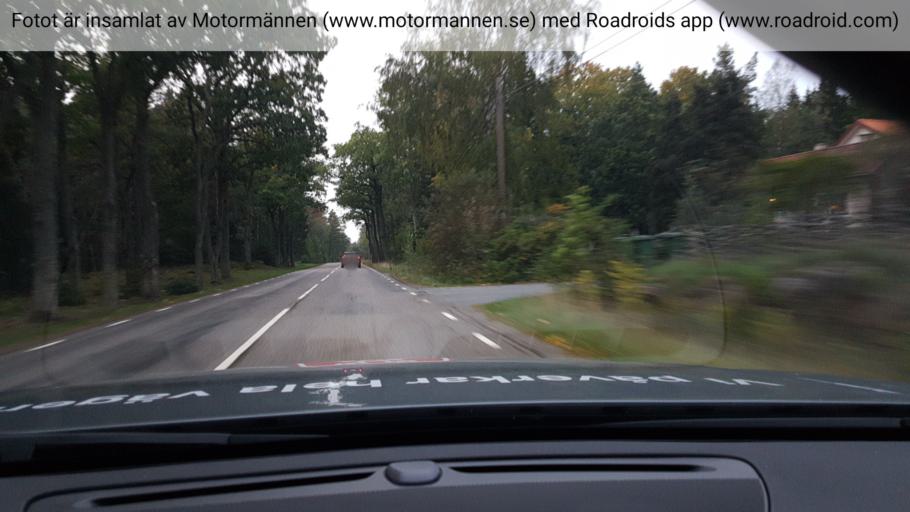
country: SE
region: Stockholm
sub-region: Haninge Kommun
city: Haninge
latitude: 59.1159
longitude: 18.1901
